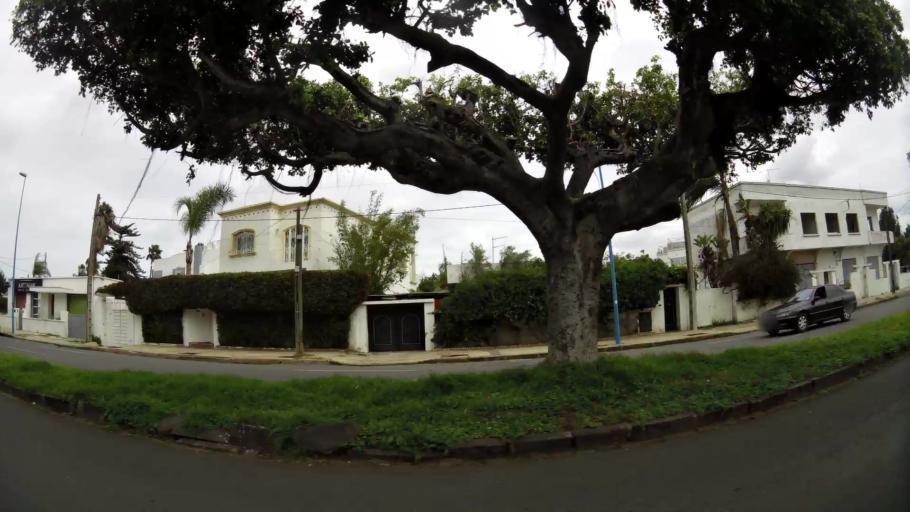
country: MA
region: Grand Casablanca
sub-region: Casablanca
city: Casablanca
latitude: 33.5576
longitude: -7.6358
